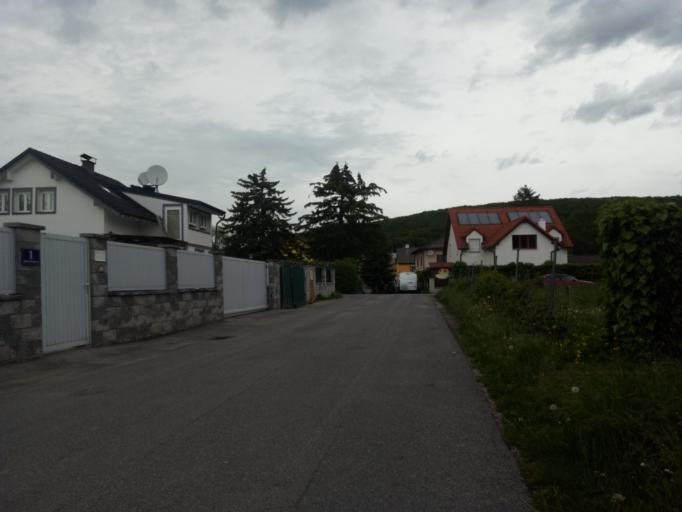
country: AT
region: Lower Austria
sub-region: Politischer Bezirk Modling
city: Kaltenleutgeben
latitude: 48.1380
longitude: 16.2001
